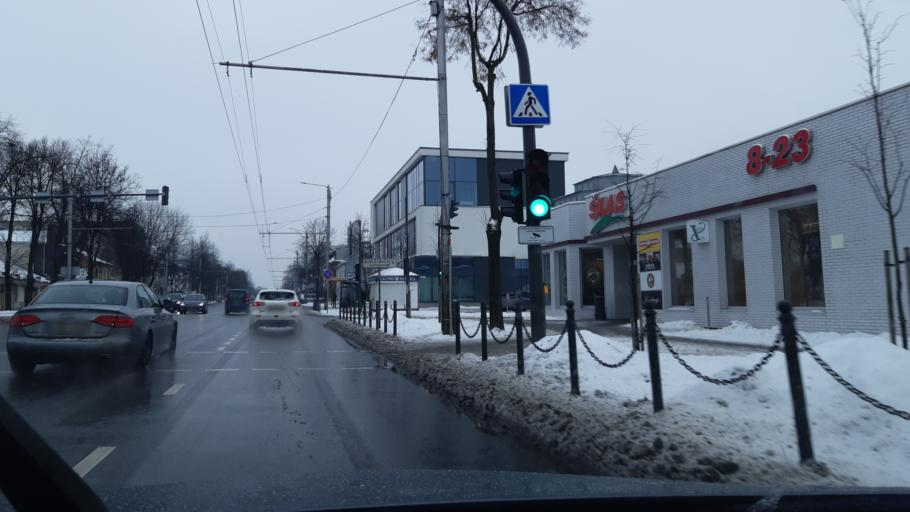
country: LT
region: Kauno apskritis
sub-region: Kaunas
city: Kaunas
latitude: 54.9054
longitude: 23.9200
